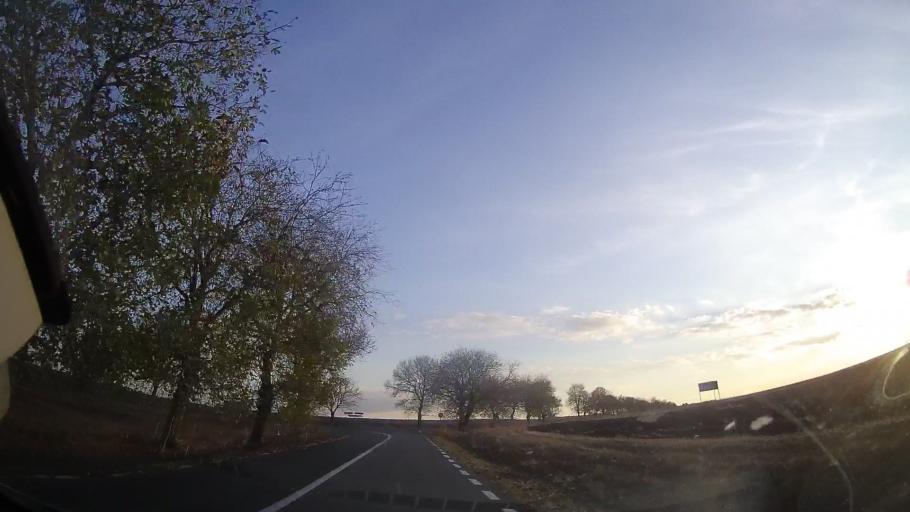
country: RO
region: Constanta
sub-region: Comuna Negru Voda
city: Negru Voda
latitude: 43.8486
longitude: 28.2378
